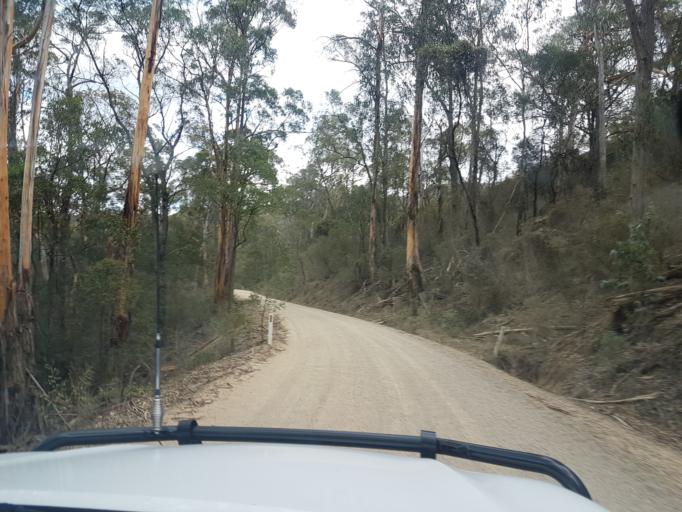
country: AU
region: Victoria
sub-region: East Gippsland
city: Bairnsdale
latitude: -37.6923
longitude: 147.5642
